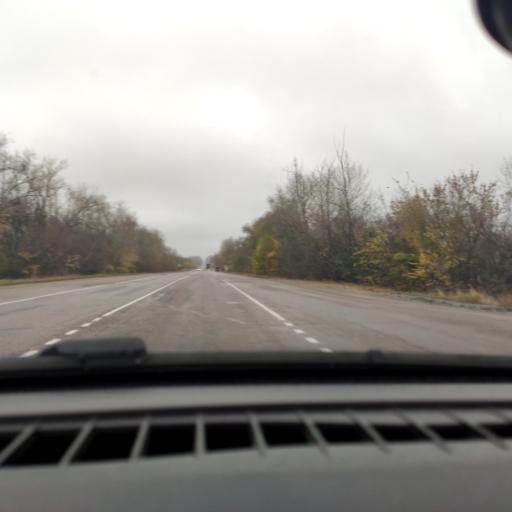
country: RU
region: Voronezj
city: Uryv-Pokrovka
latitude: 51.1474
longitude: 39.0594
